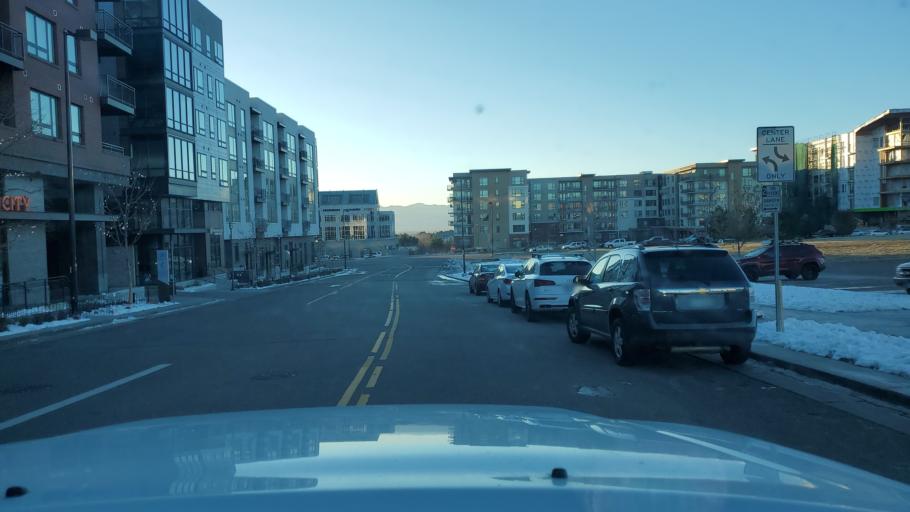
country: US
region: Colorado
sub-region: Arapahoe County
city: Castlewood
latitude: 39.6255
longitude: -104.9074
